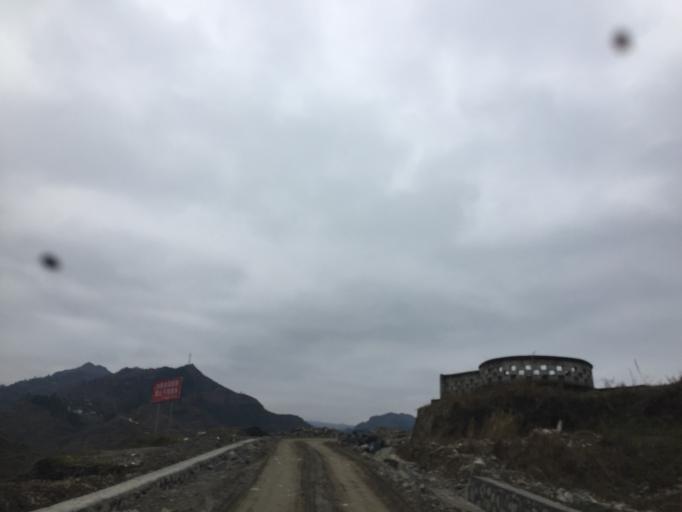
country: CN
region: Guizhou Sheng
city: Changfeng
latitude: 28.4391
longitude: 108.0789
